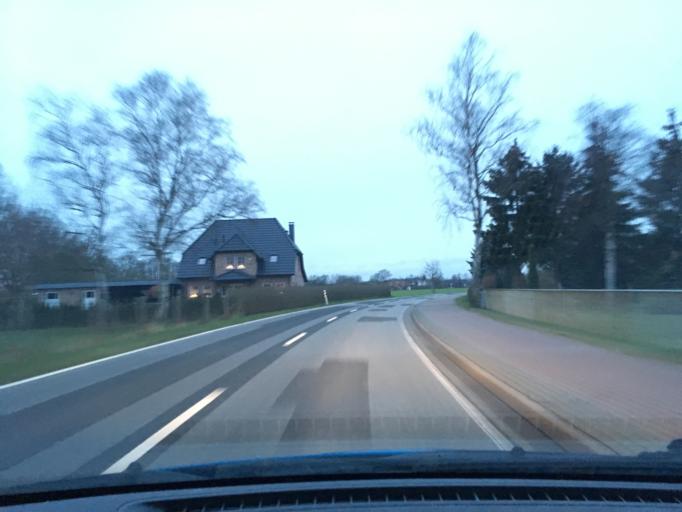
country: DE
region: Mecklenburg-Vorpommern
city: Boizenburg
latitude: 53.3658
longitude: 10.7616
